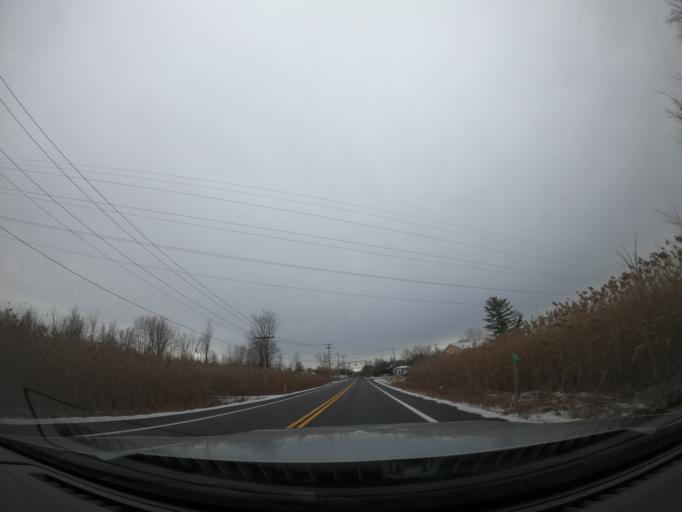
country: US
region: New York
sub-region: Madison County
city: Bridgeport
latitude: 43.1243
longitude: -75.9969
